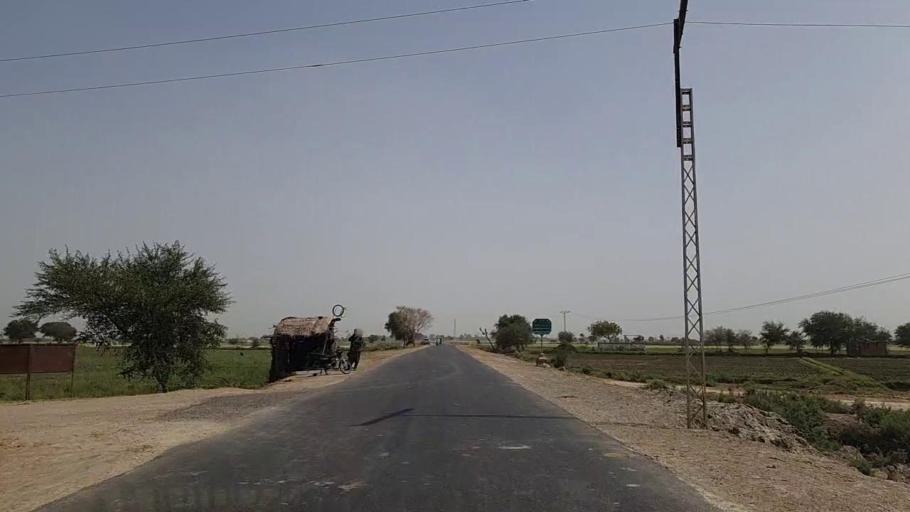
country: PK
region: Sindh
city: Tando Bago
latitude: 24.8255
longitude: 68.8980
